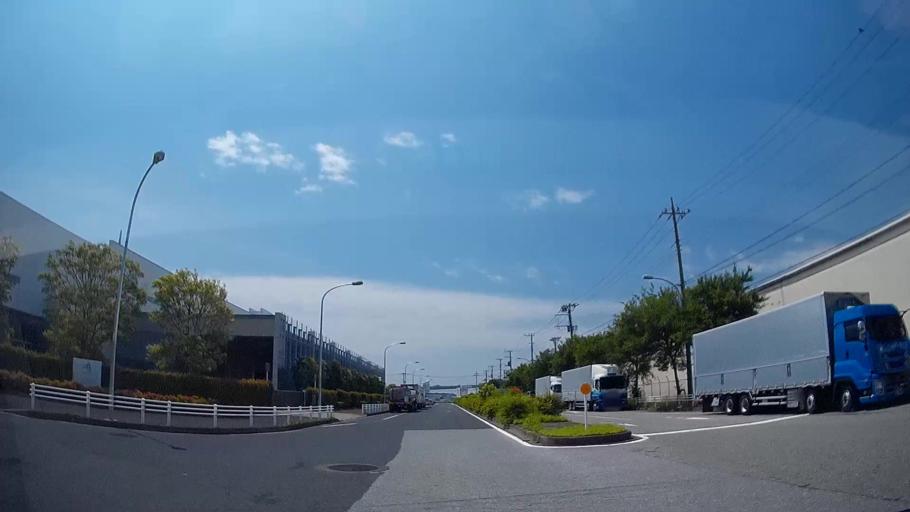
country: JP
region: Tokyo
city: Urayasu
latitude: 35.6245
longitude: 139.8314
